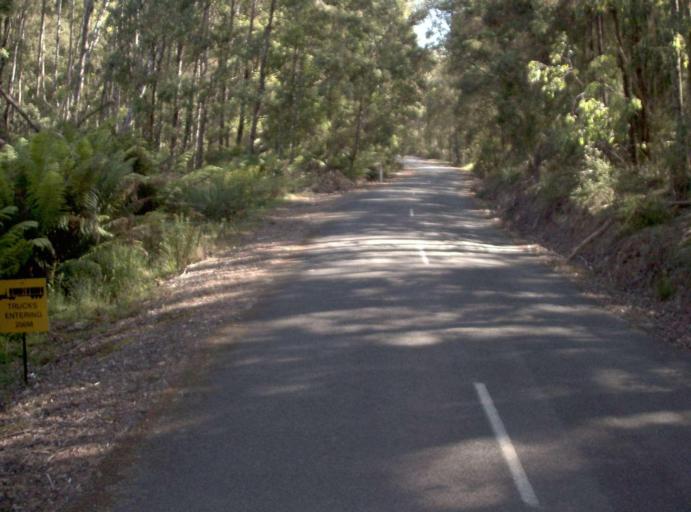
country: AU
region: Victoria
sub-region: East Gippsland
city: Lakes Entrance
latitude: -37.3934
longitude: 148.5957
